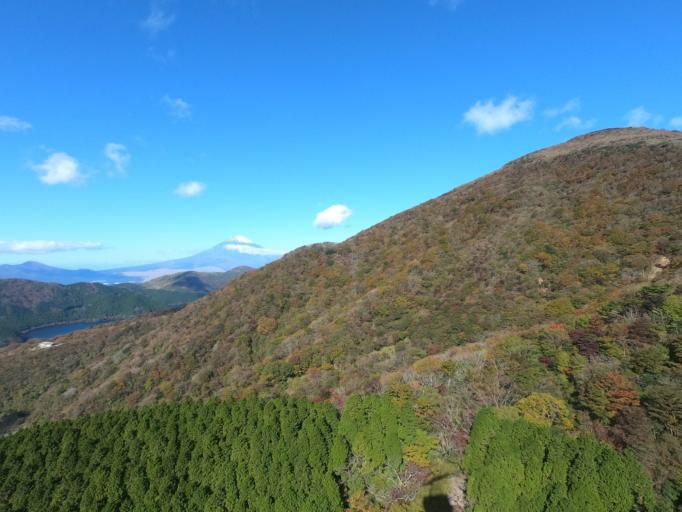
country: JP
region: Kanagawa
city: Hakone
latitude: 35.2197
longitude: 139.0186
